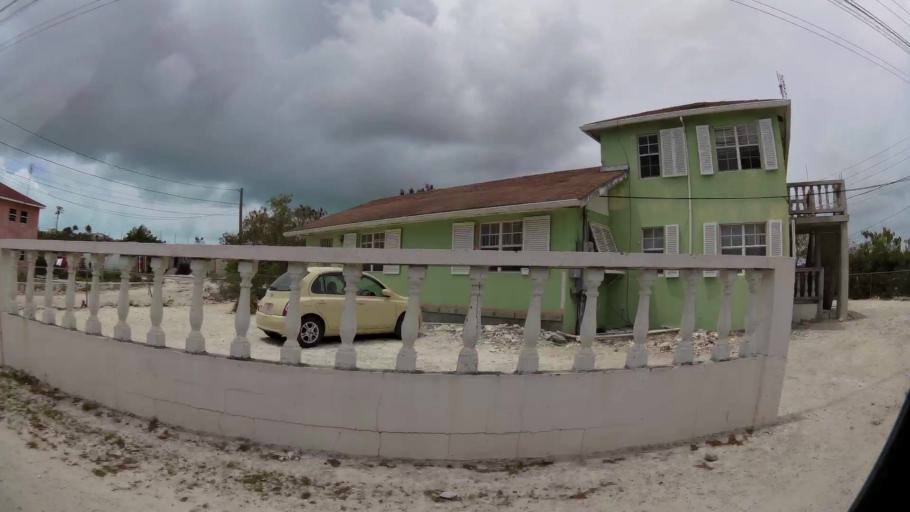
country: BS
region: Mayaguana
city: Abraham's Bay
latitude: 21.7844
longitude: -72.2586
